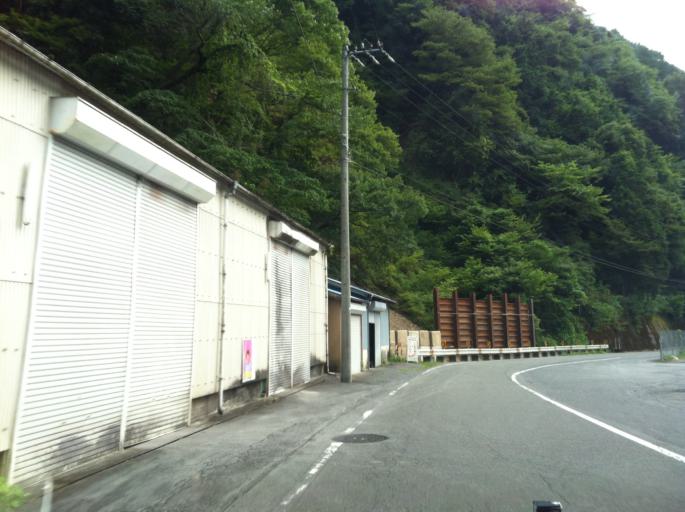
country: JP
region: Shizuoka
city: Shizuoka-shi
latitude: 35.2459
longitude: 138.3445
